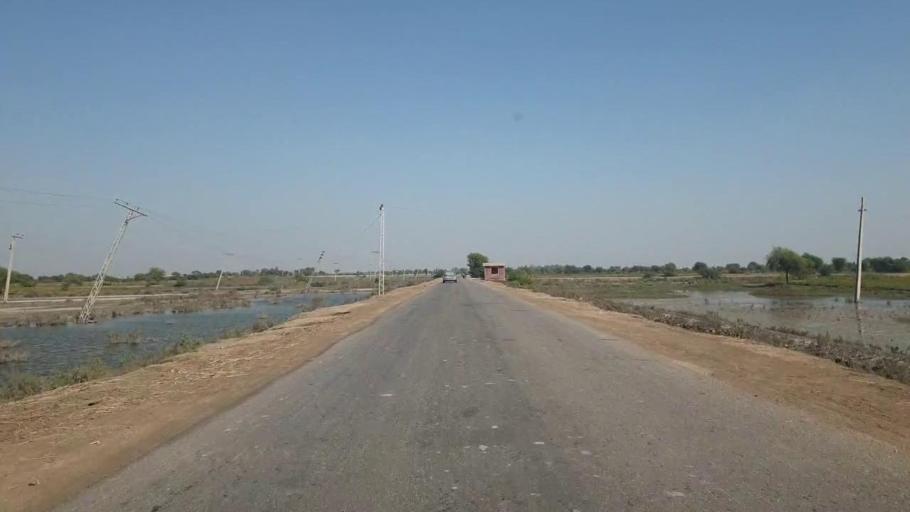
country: PK
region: Sindh
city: Talhar
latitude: 24.9085
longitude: 68.8436
